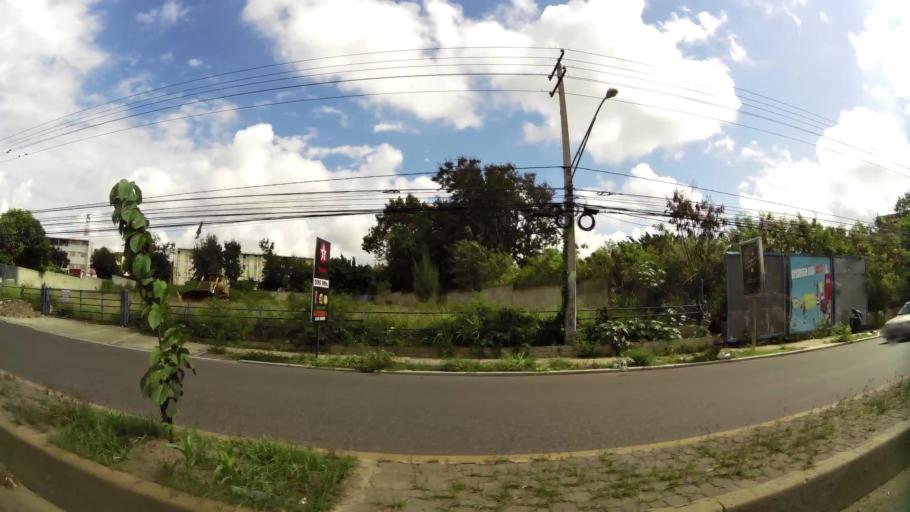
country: DO
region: Santiago
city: Santiago de los Caballeros
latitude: 19.4781
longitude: -70.7004
